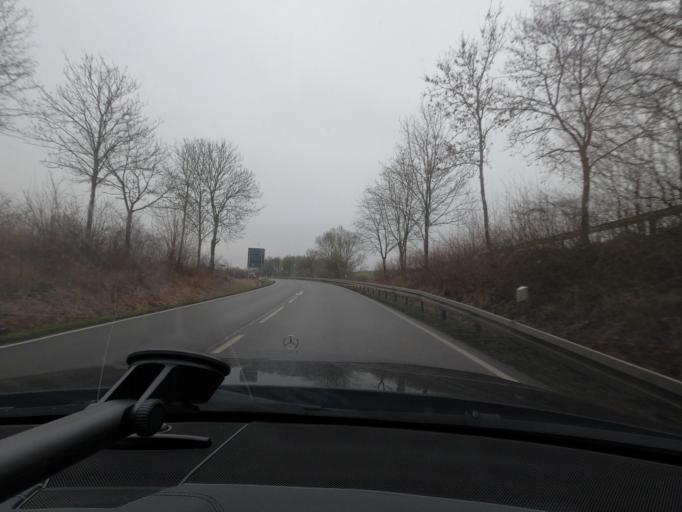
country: DE
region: Hesse
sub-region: Regierungsbezirk Kassel
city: Volkmarsen
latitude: 51.3395
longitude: 9.0970
